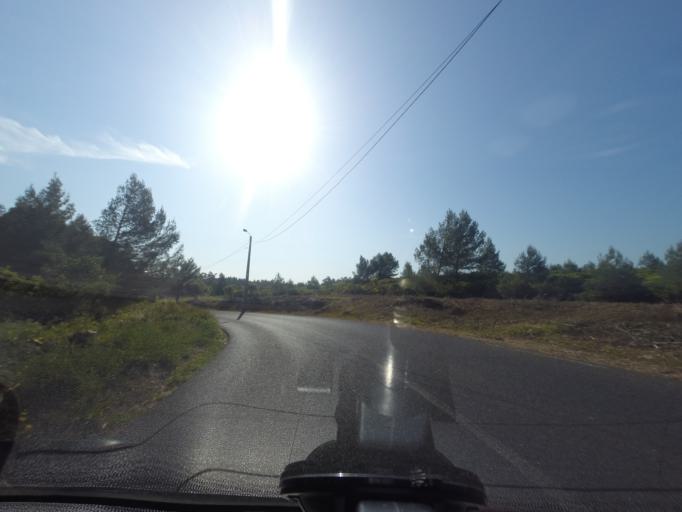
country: PT
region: Lisbon
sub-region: Cascais
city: Alcabideche
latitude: 38.7415
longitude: -9.4282
